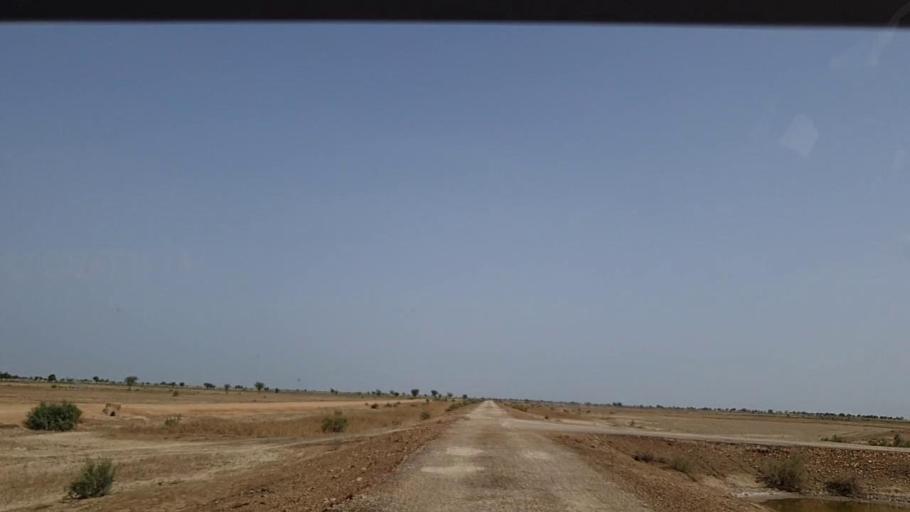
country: PK
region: Sindh
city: Johi
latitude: 26.7827
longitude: 67.6483
